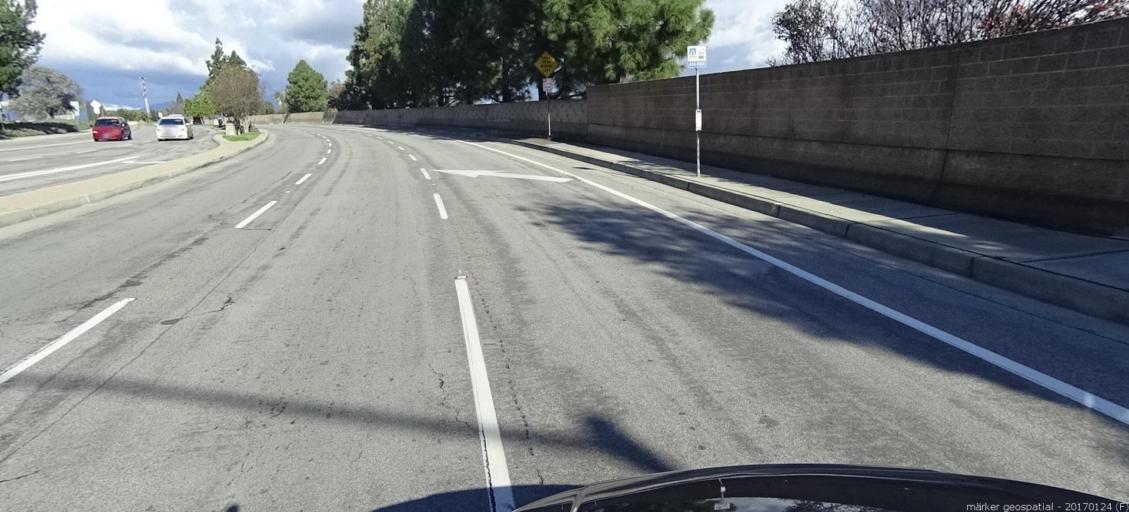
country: US
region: California
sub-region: Orange County
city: Laguna Hills
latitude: 33.6065
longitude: -117.6993
